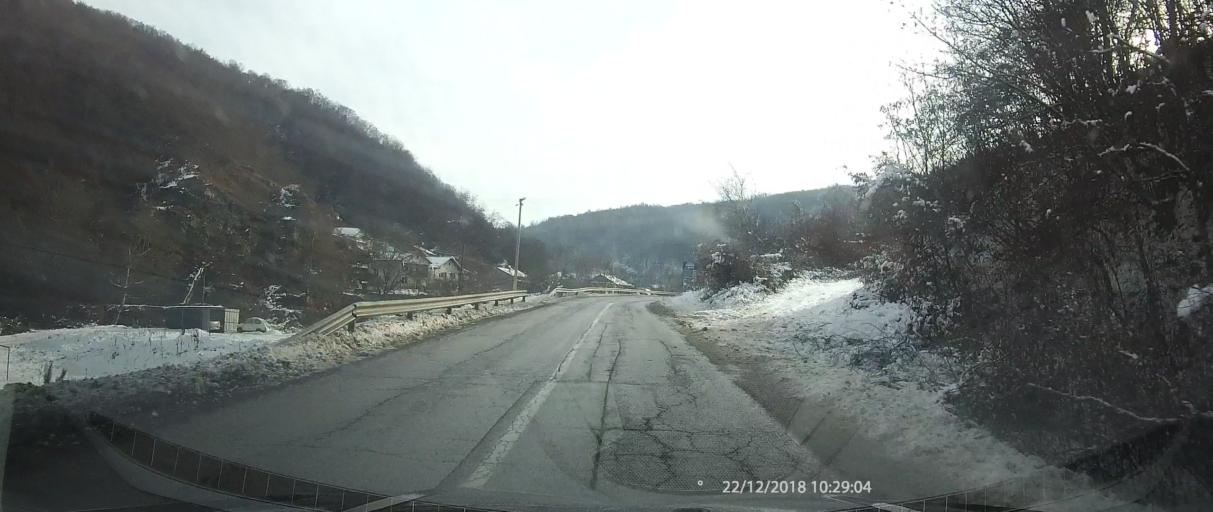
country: MK
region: Kriva Palanka
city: Kriva Palanka
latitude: 42.2244
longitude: 22.3918
